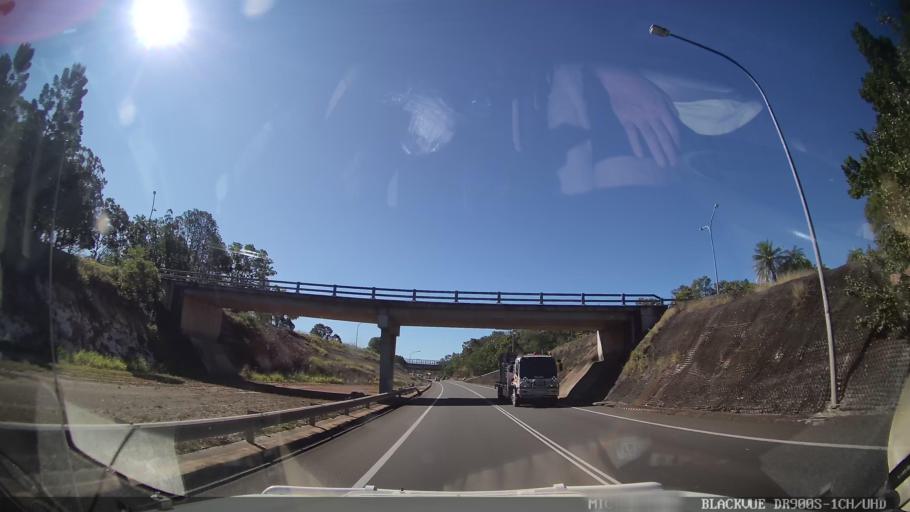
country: AU
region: Queensland
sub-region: Fraser Coast
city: Maryborough
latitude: -25.5194
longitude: 152.6686
